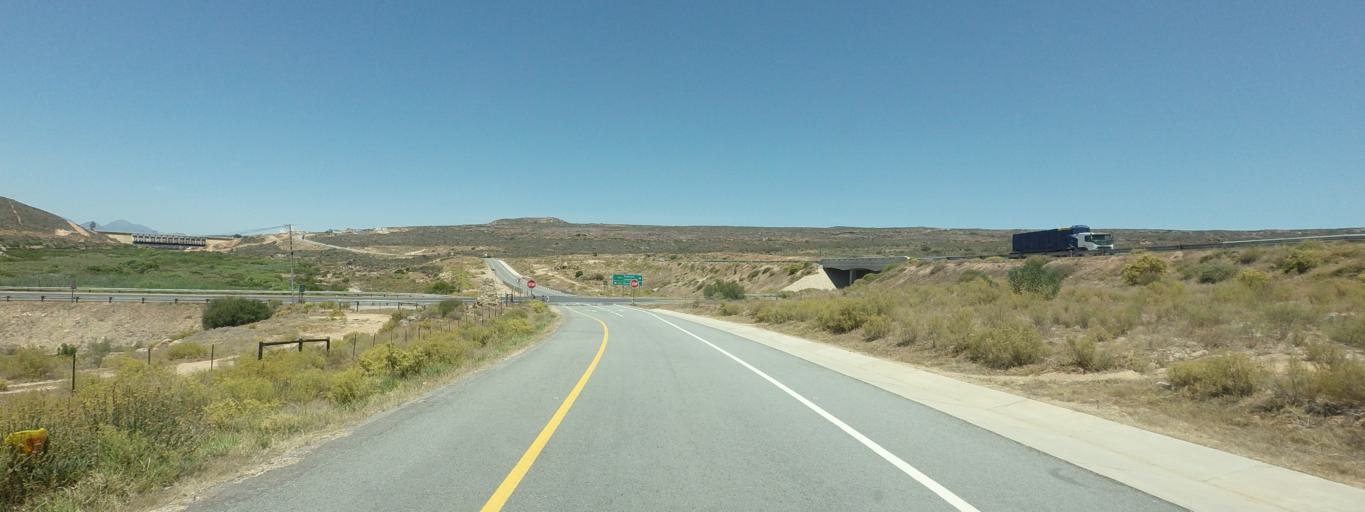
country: ZA
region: Western Cape
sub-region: West Coast District Municipality
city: Clanwilliam
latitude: -32.1723
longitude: 18.8683
